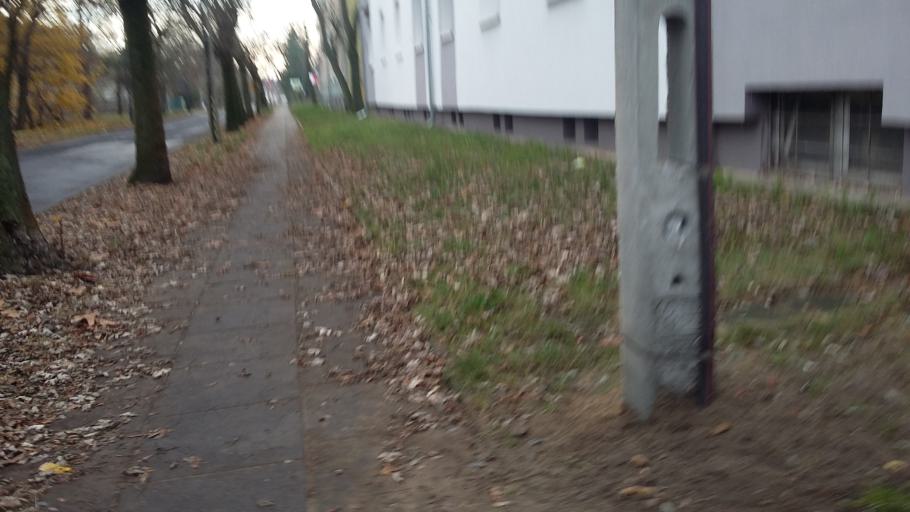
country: PL
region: Lodz Voivodeship
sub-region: Powiat pabianicki
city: Ksawerow
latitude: 51.7136
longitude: 19.4226
